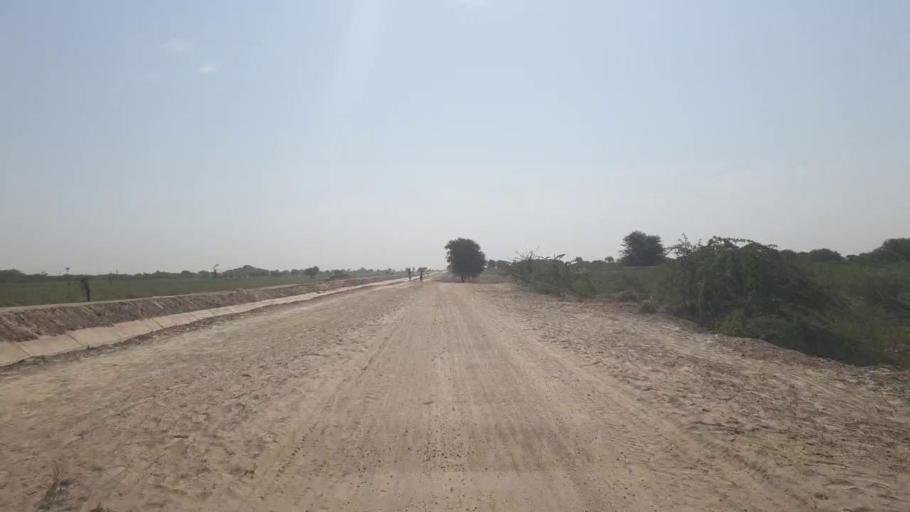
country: PK
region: Sindh
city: Kunri
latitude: 25.2679
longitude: 69.6282
